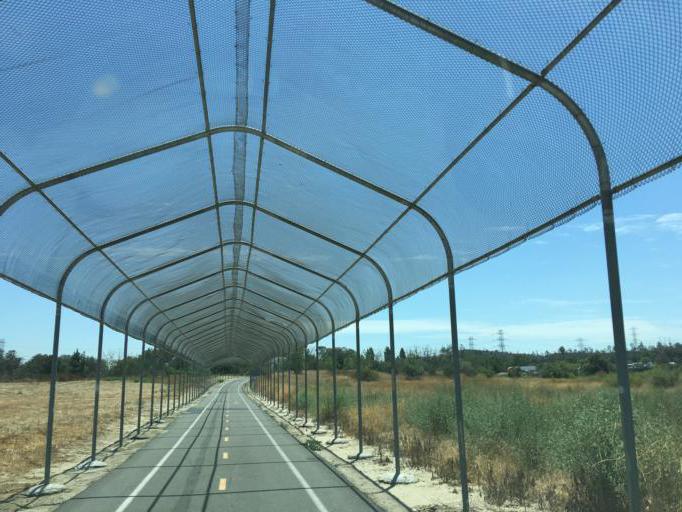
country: US
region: California
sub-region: Los Angeles County
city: South El Monte
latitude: 34.0445
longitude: -118.0716
